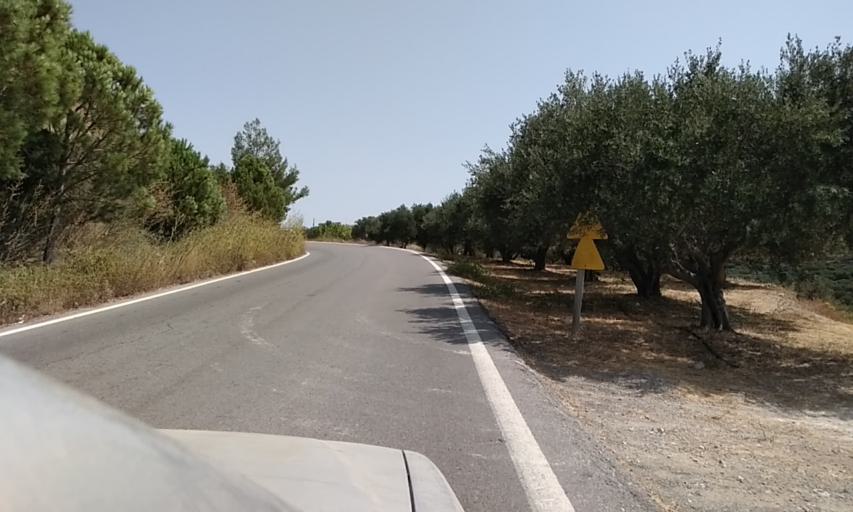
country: GR
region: Crete
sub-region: Nomos Lasithiou
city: Makry-Gialos
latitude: 35.0987
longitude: 26.0636
